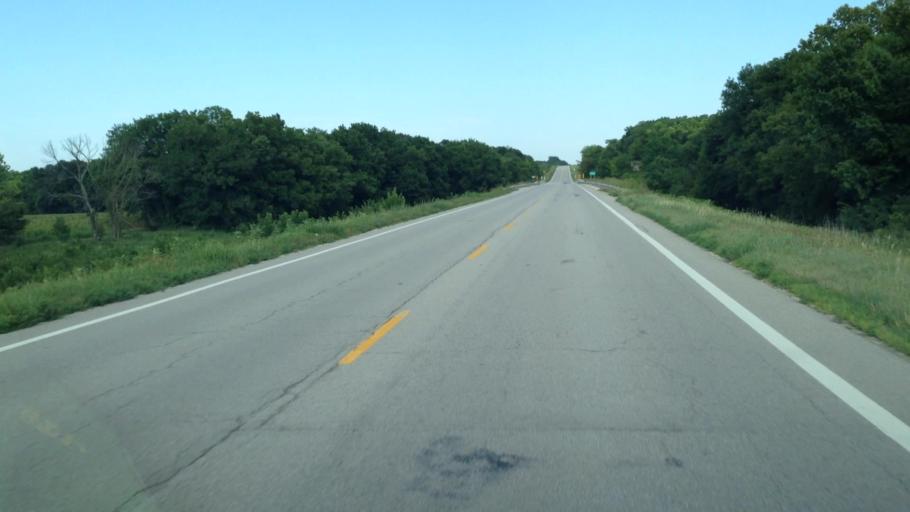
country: US
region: Kansas
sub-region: Neosho County
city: Erie
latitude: 37.6882
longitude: -95.2009
